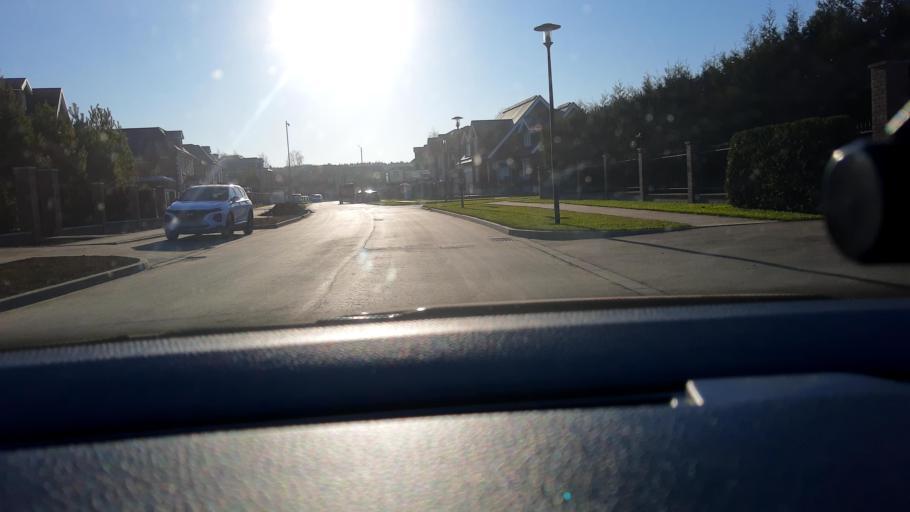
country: RU
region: Moskovskaya
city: Barvikha
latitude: 55.7519
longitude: 37.3052
